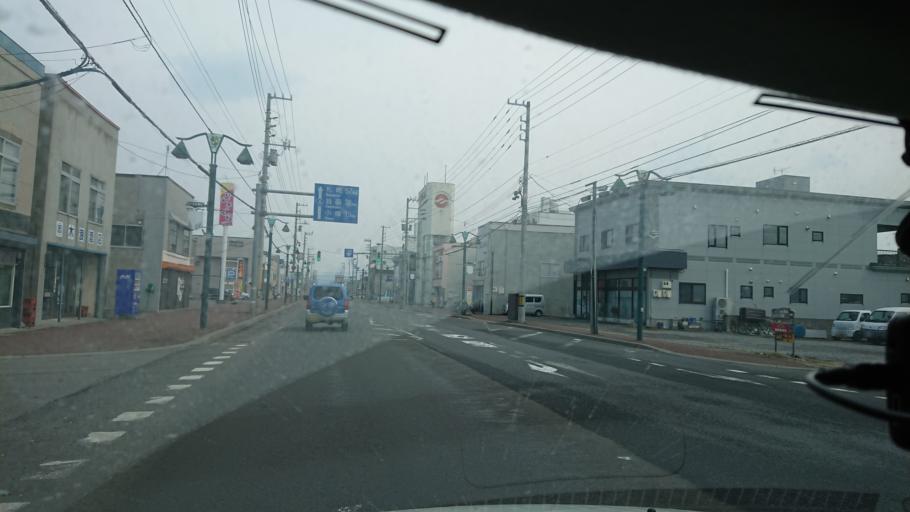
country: JP
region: Hokkaido
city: Yoichi
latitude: 43.1922
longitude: 140.7954
